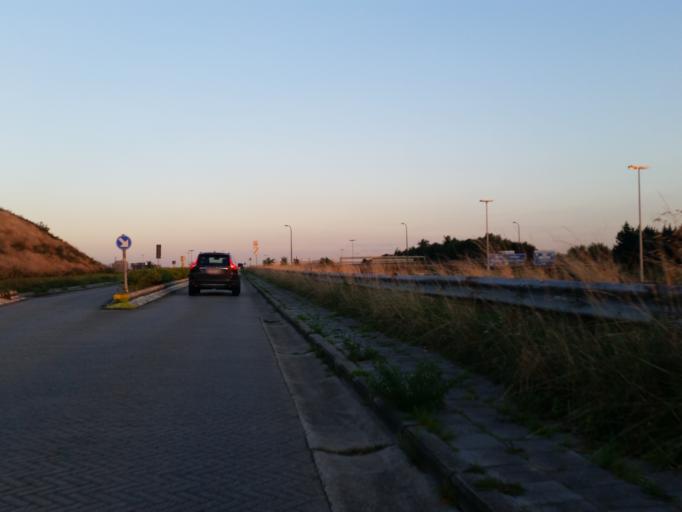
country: BE
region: Flanders
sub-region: Provincie Vlaams-Brabant
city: Diegem
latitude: 50.8987
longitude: 4.4426
